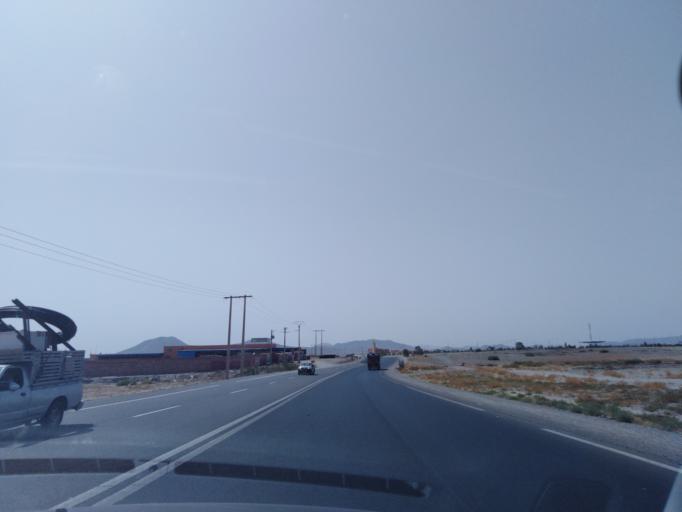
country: MA
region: Marrakech-Tensift-Al Haouz
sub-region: Marrakech
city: Marrakesh
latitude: 31.7700
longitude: -8.1260
